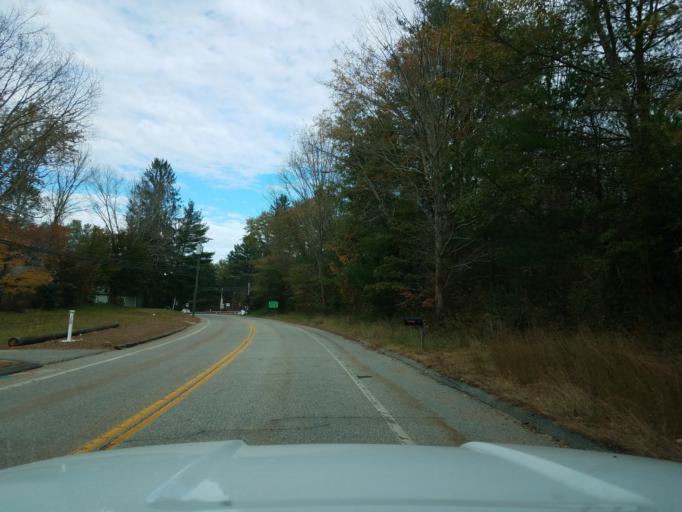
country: US
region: Connecticut
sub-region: Tolland County
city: Storrs
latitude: 41.8627
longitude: -72.1600
